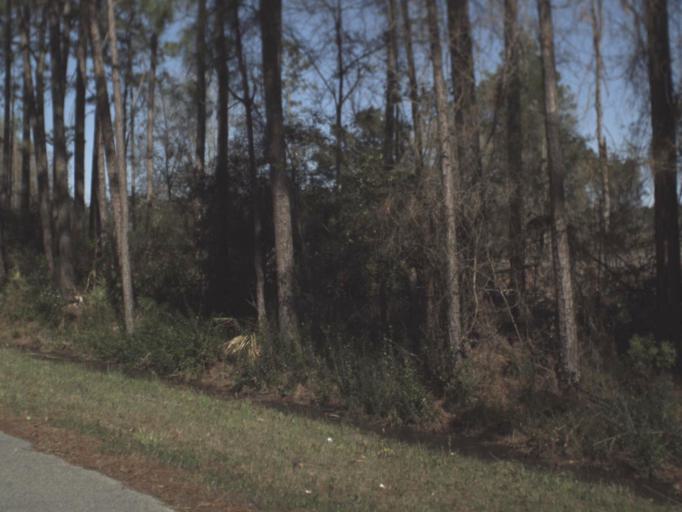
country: US
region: Florida
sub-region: Gulf County
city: Wewahitchka
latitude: 29.9546
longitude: -85.1793
